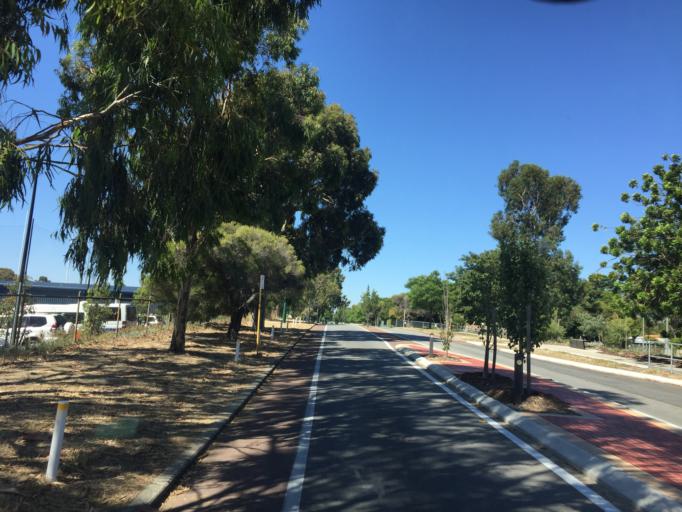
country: AU
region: Western Australia
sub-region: Victoria Park
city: Victoria Park
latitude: -31.9743
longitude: 115.9088
